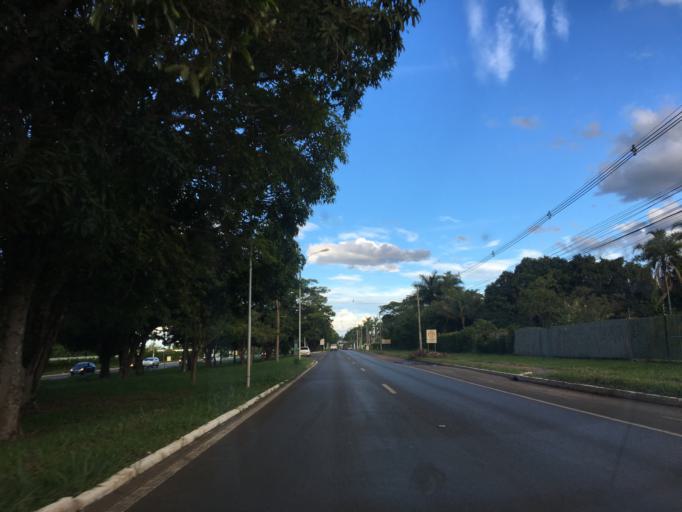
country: BR
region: Federal District
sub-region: Brasilia
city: Brasilia
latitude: -15.8576
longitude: -47.9226
